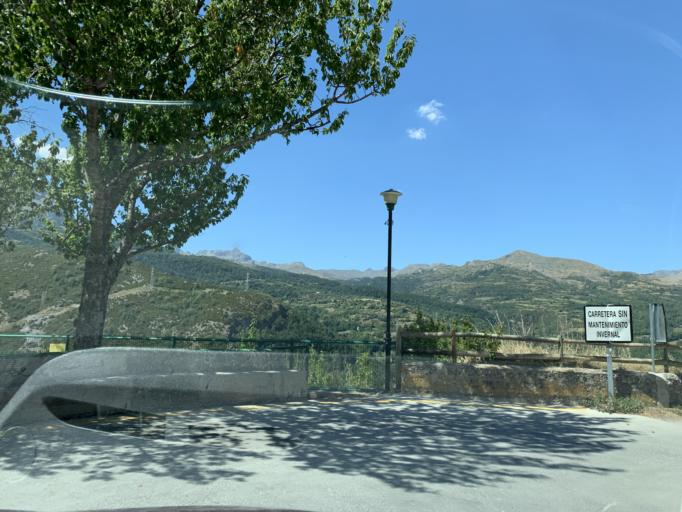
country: ES
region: Aragon
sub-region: Provincia de Huesca
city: Hoz de Jaca
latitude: 42.6903
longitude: -0.3106
